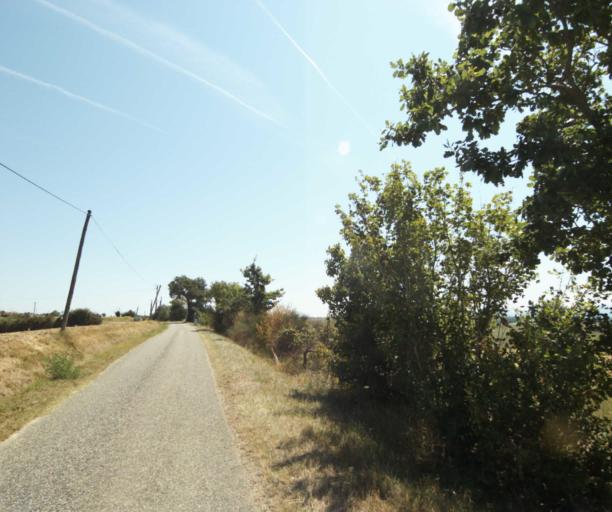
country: FR
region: Midi-Pyrenees
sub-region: Departement de l'Ariege
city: Lezat-sur-Leze
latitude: 43.3078
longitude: 1.3505
